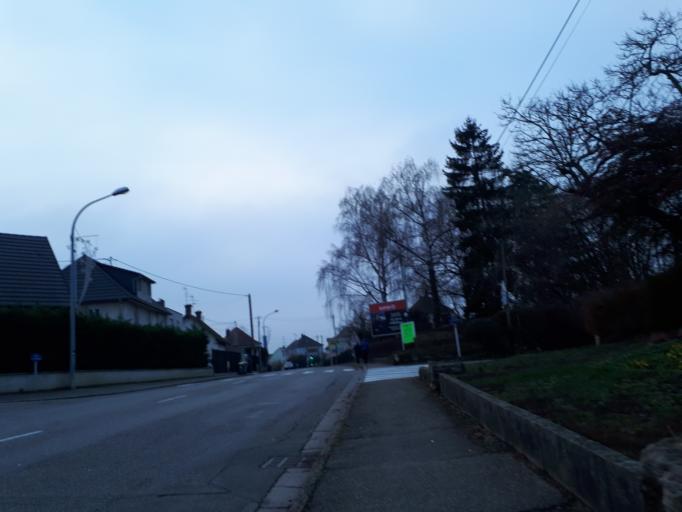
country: FR
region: Alsace
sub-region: Departement du Haut-Rhin
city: Morschwiller-le-Bas
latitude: 47.7370
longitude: 7.2753
